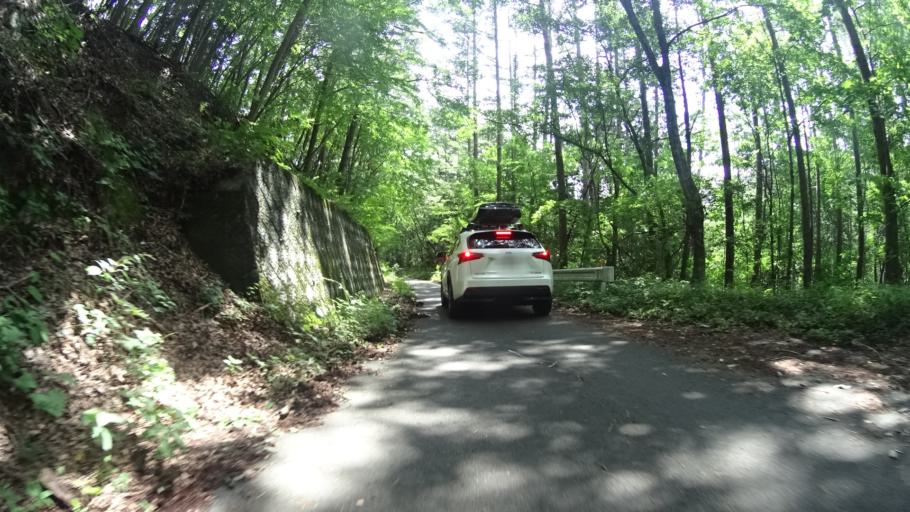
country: JP
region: Yamanashi
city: Nirasaki
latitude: 35.8824
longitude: 138.5021
